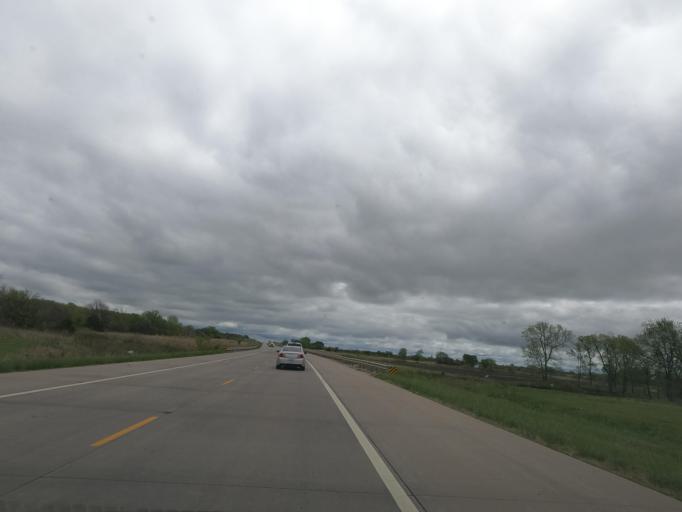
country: US
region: Kansas
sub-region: Elk County
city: Howard
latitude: 37.6348
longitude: -96.2245
